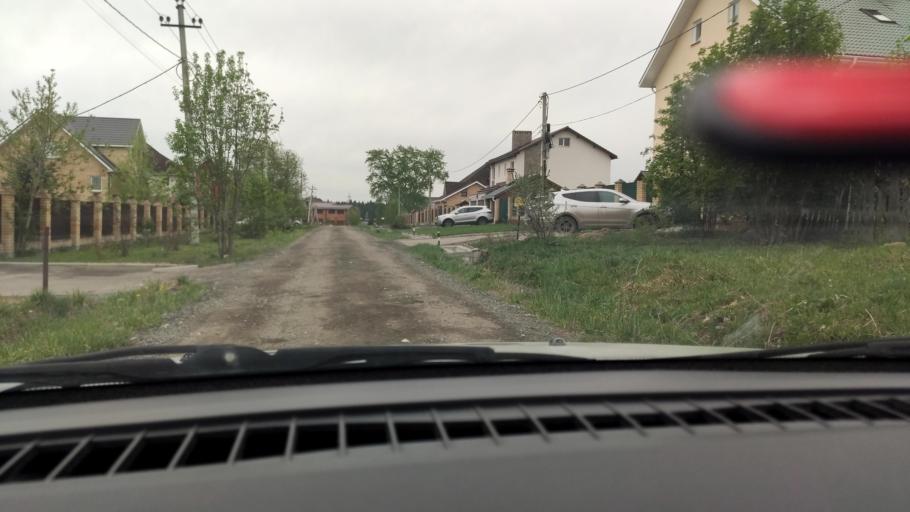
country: RU
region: Perm
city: Perm
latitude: 57.9974
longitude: 56.3401
